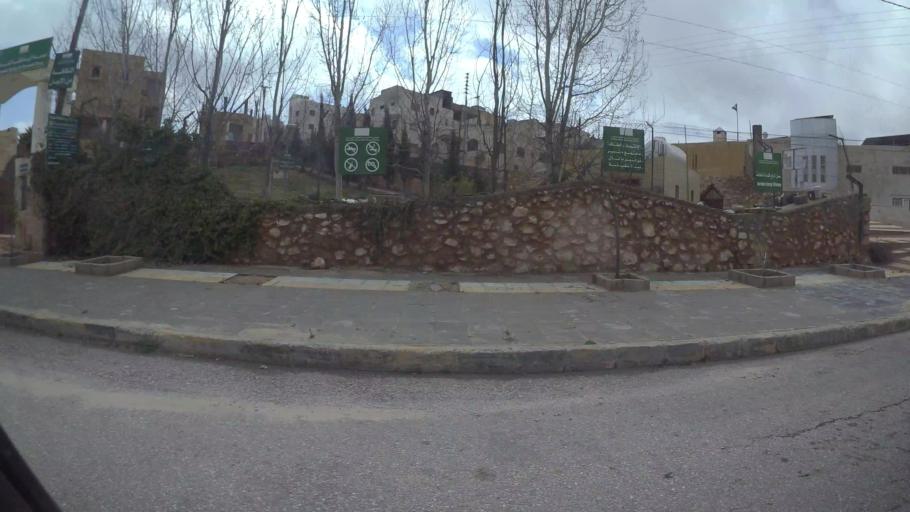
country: JO
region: Amman
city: Al Jubayhah
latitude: 32.0703
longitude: 35.8846
